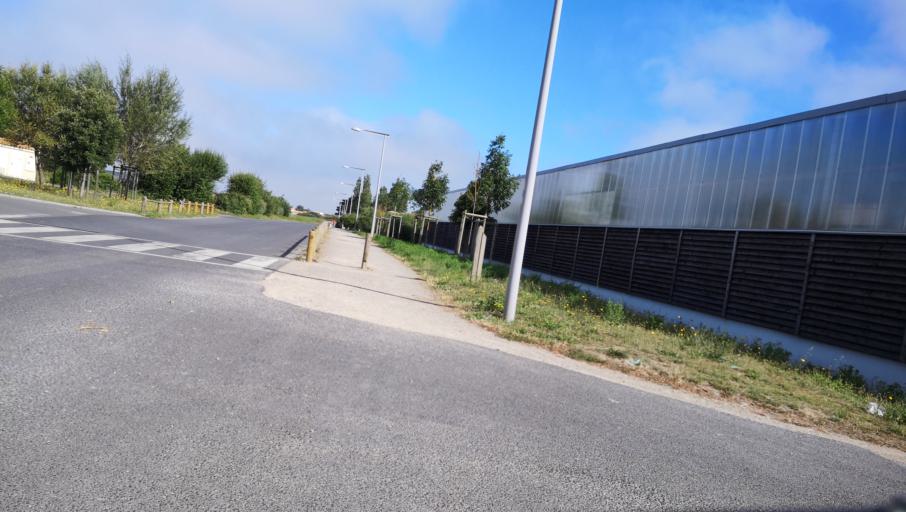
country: FR
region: Pays de la Loire
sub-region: Departement de la Vendee
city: Les Sables-d'Olonne
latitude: 46.5070
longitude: -1.7883
